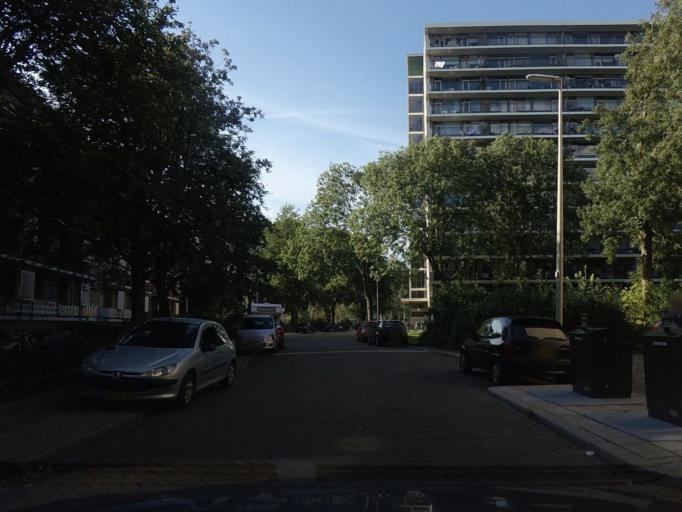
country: NL
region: South Holland
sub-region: Gemeente Leidschendam-Voorburg
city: Voorburg
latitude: 52.0947
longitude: 4.3694
